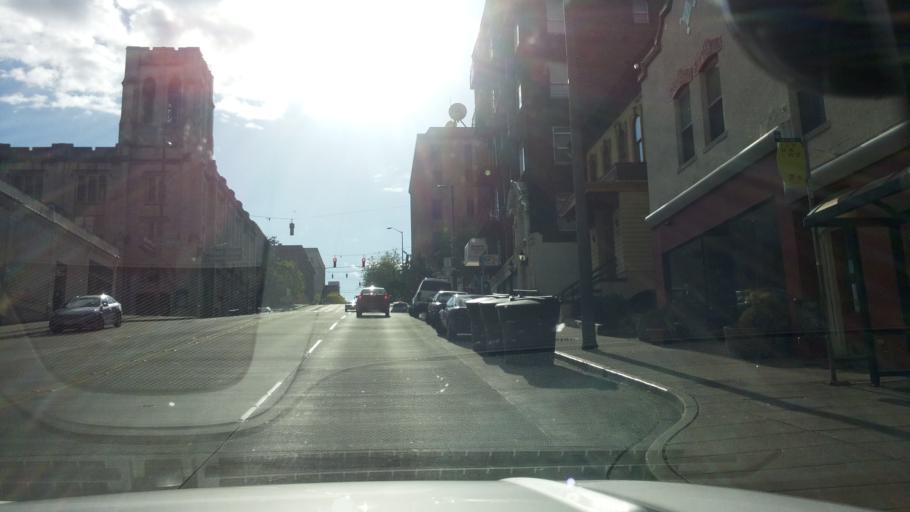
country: US
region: Washington
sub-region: Pierce County
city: Tacoma
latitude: 47.2554
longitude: -122.4410
